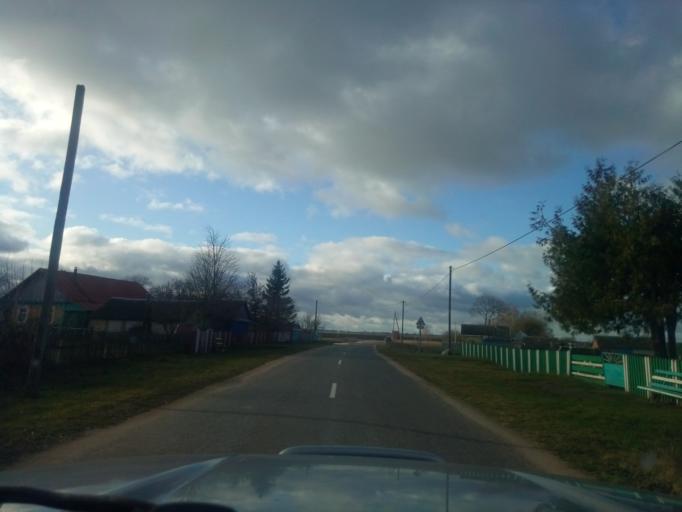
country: BY
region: Minsk
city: Tsimkavichy
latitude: 53.1972
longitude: 26.9285
